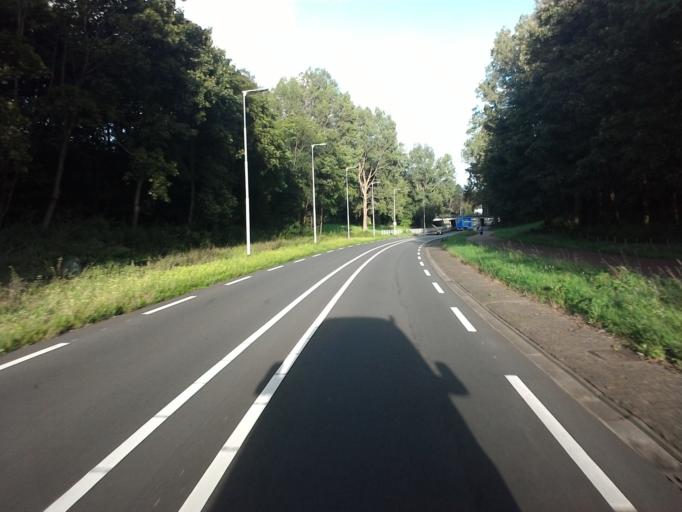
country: NL
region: North Holland
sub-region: Gemeente Beverwijk
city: Beverwijk
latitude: 52.4883
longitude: 4.6246
